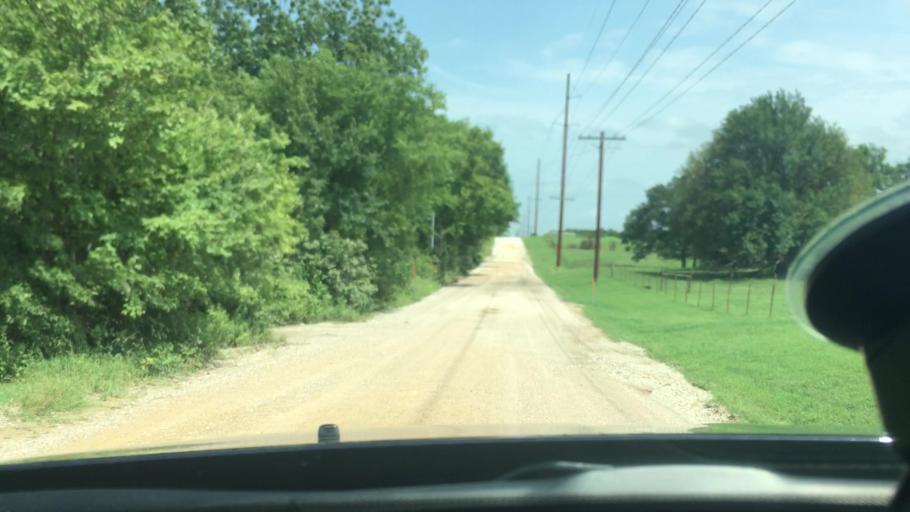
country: US
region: Oklahoma
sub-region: Pontotoc County
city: Ada
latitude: 34.8255
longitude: -96.7371
